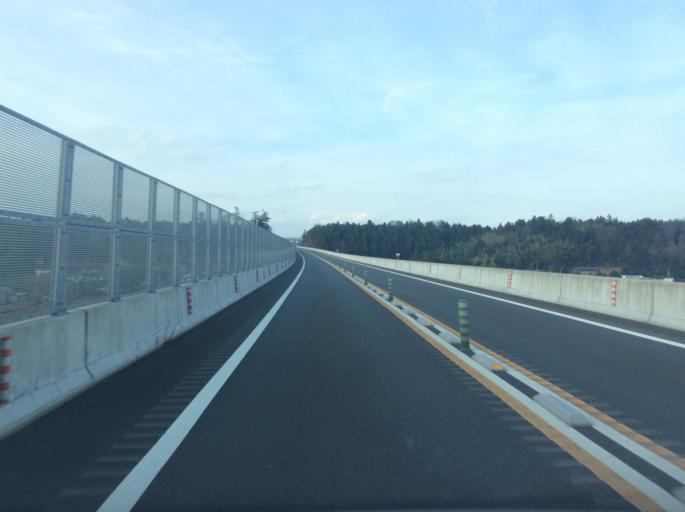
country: JP
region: Fukushima
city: Namie
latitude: 37.4754
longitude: 140.9597
